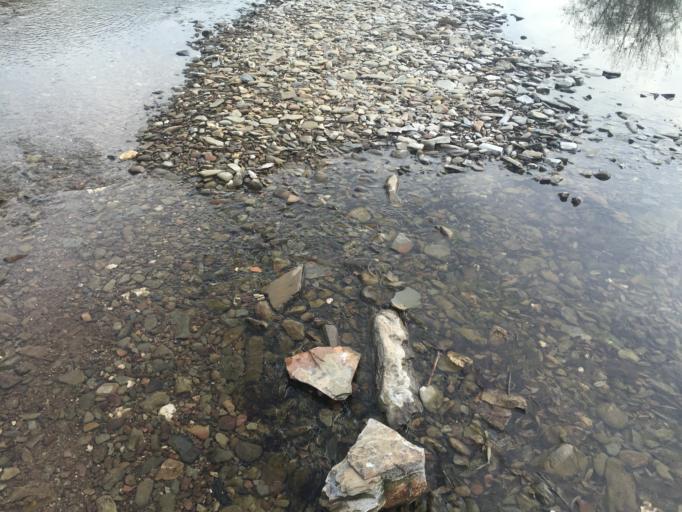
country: PT
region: Faro
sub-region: Tavira
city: Tavira
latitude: 37.2931
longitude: -7.6062
